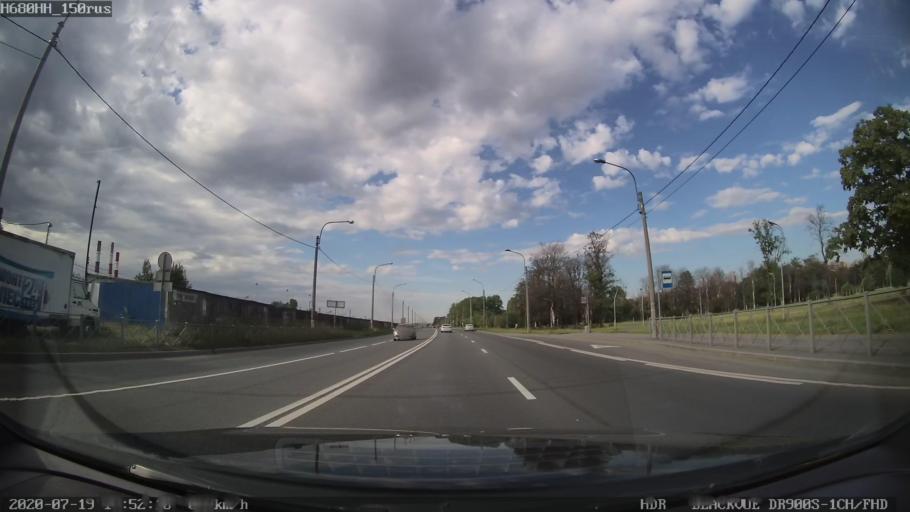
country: RU
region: St.-Petersburg
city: Avtovo
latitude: 59.8647
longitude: 30.2954
